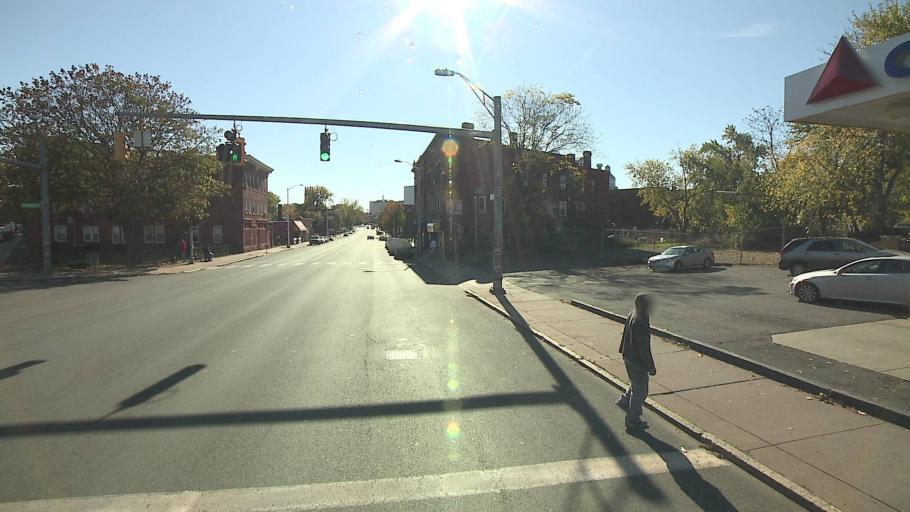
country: US
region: Connecticut
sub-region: Hartford County
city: Hartford
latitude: 41.7759
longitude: -72.6802
